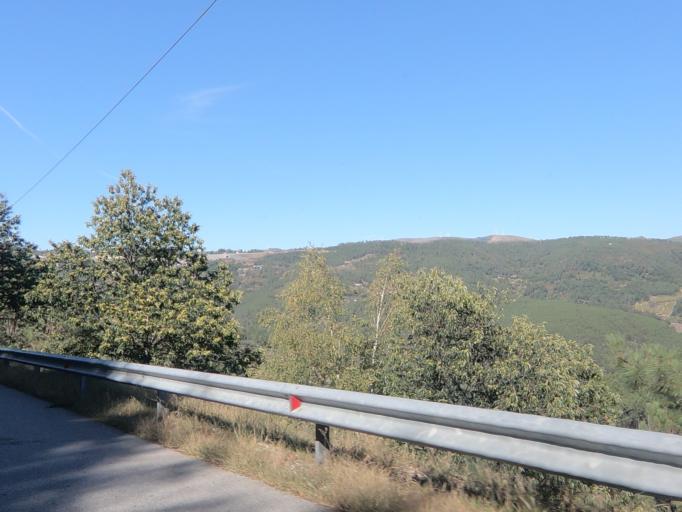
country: PT
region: Vila Real
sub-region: Santa Marta de Penaguiao
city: Santa Marta de Penaguiao
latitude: 41.2529
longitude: -7.8530
